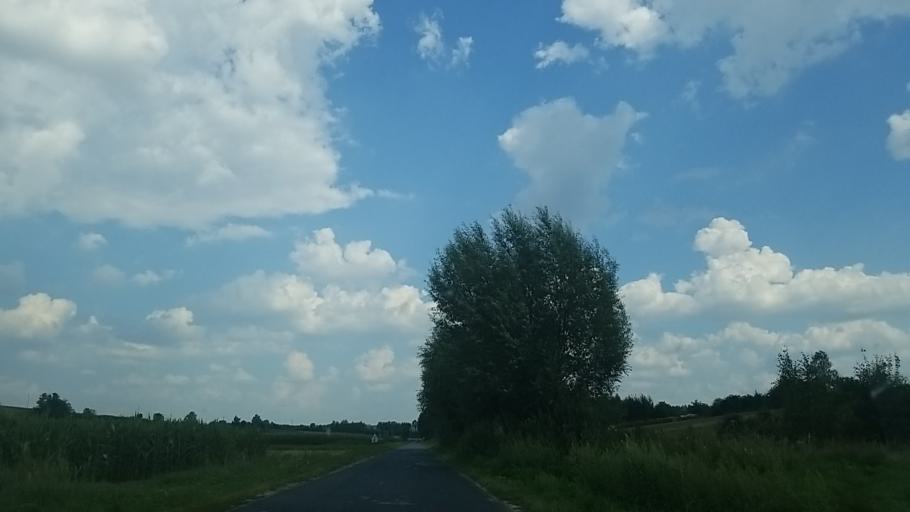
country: PL
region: Lublin Voivodeship
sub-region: Powiat bilgorajski
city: Goraj
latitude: 50.7259
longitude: 22.6415
